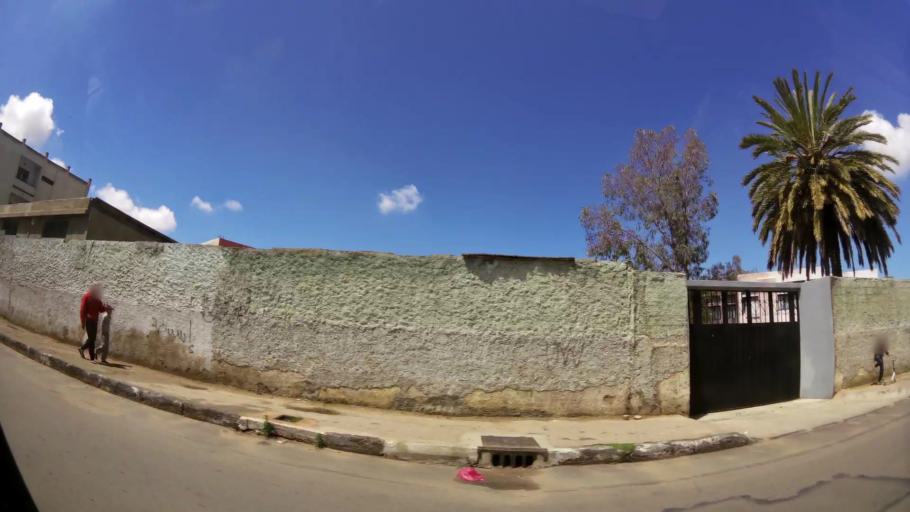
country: MA
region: Grand Casablanca
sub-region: Casablanca
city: Casablanca
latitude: 33.5616
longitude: -7.5774
